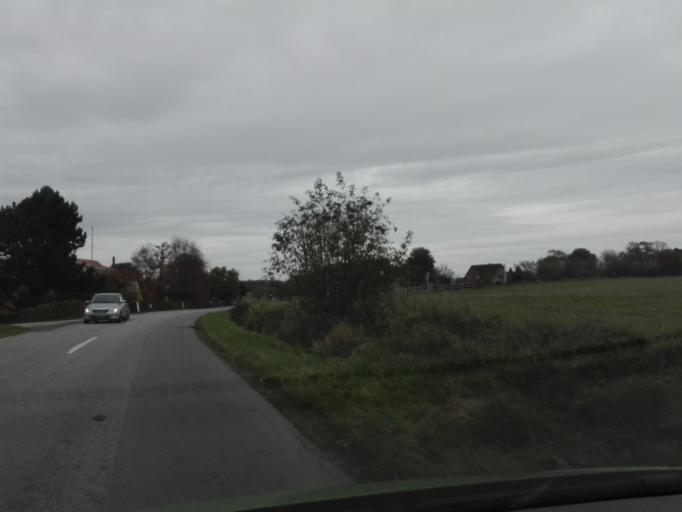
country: DK
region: Central Jutland
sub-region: Arhus Kommune
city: Solbjerg
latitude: 56.0665
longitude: 10.0966
